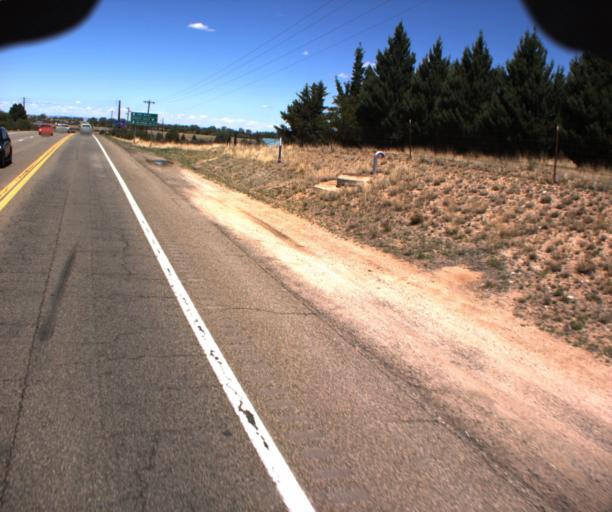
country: US
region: Arizona
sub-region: Yavapai County
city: Prescott
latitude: 34.6270
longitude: -112.4275
